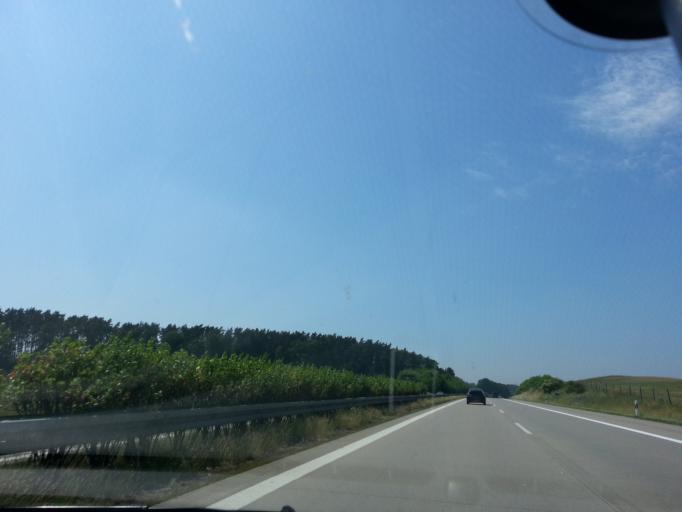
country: DE
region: Mecklenburg-Vorpommern
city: Siggelkow
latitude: 53.2995
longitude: 11.9395
